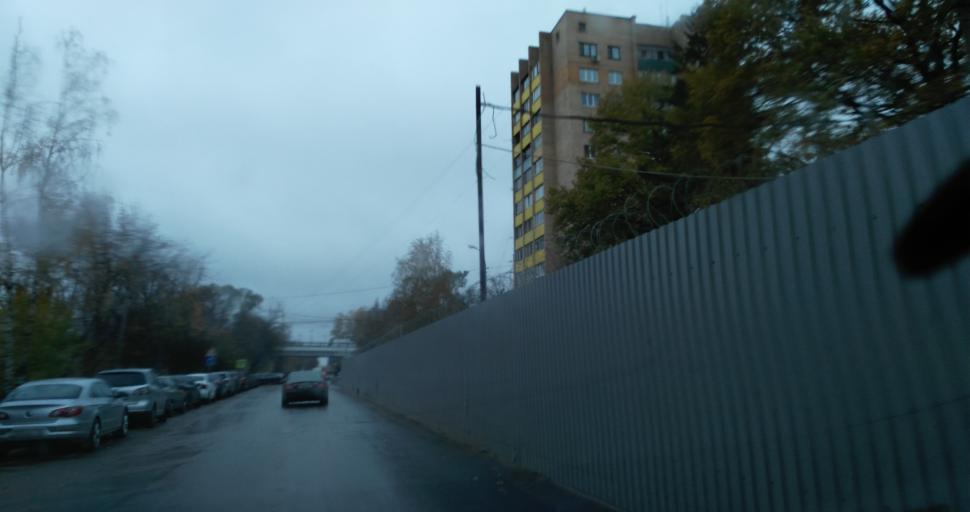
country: RU
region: Moscow
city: Khimki
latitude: 55.8956
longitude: 37.4509
